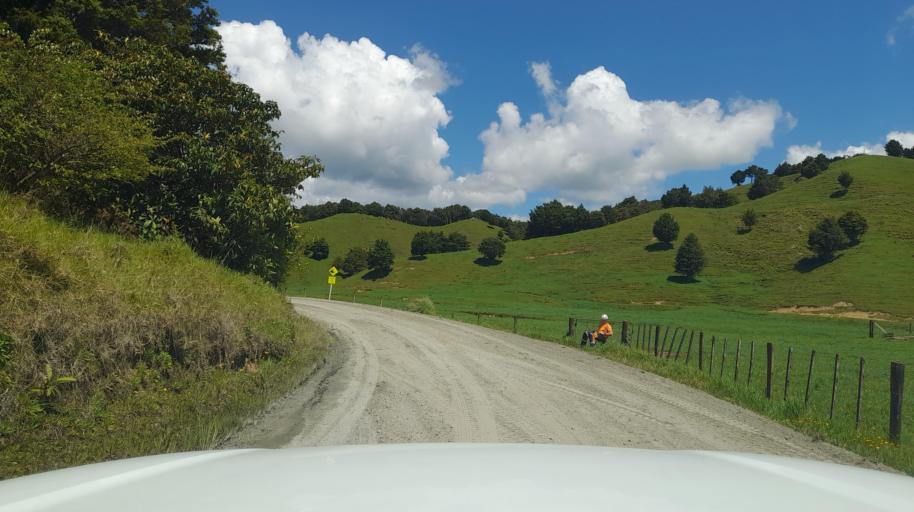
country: NZ
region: Northland
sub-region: Far North District
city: Kaitaia
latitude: -35.1074
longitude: 173.3922
